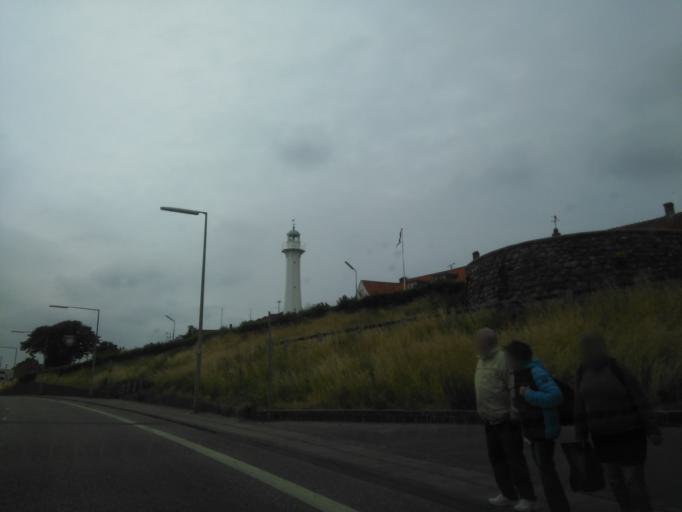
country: DK
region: Capital Region
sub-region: Bornholm Kommune
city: Ronne
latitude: 55.0989
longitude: 14.6965
